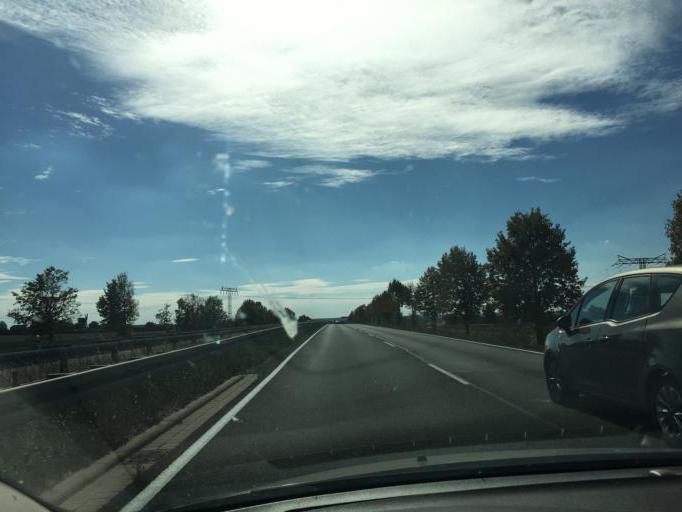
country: DE
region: Saxony-Anhalt
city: Wolmirstedt
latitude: 52.2594
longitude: 11.6128
